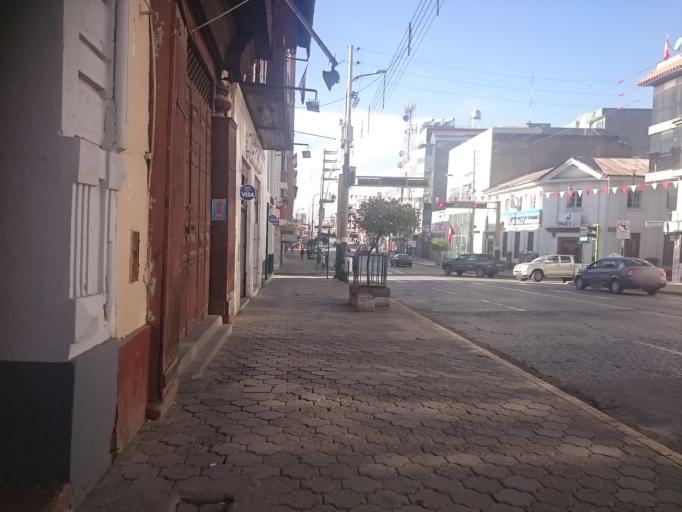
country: PE
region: Junin
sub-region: Provincia de Huancayo
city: Huancayo
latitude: -12.0691
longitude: -75.2099
